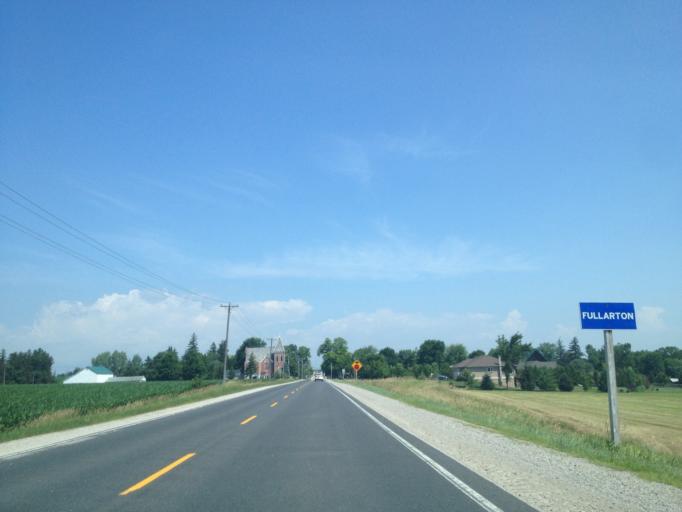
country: CA
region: Ontario
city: Huron East
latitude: 43.3860
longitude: -81.2211
